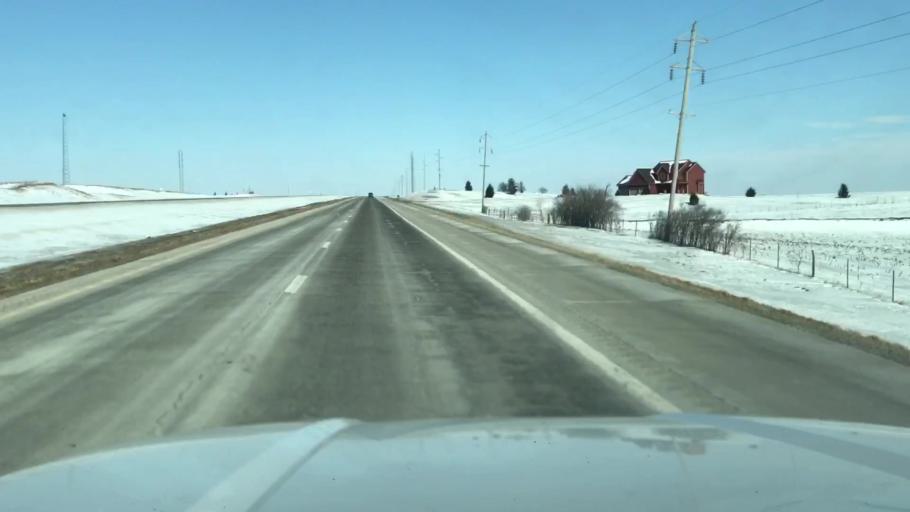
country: US
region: Missouri
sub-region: Nodaway County
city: Maryville
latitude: 40.2230
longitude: -94.8678
